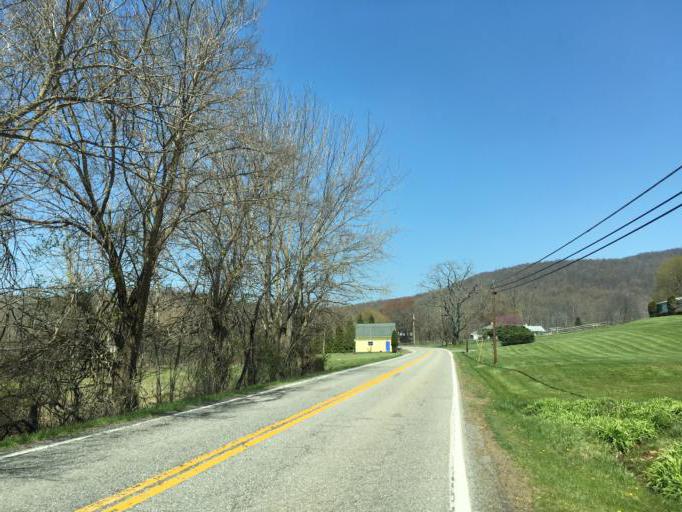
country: US
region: Maryland
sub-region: Frederick County
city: Myersville
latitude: 39.5599
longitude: -77.5244
